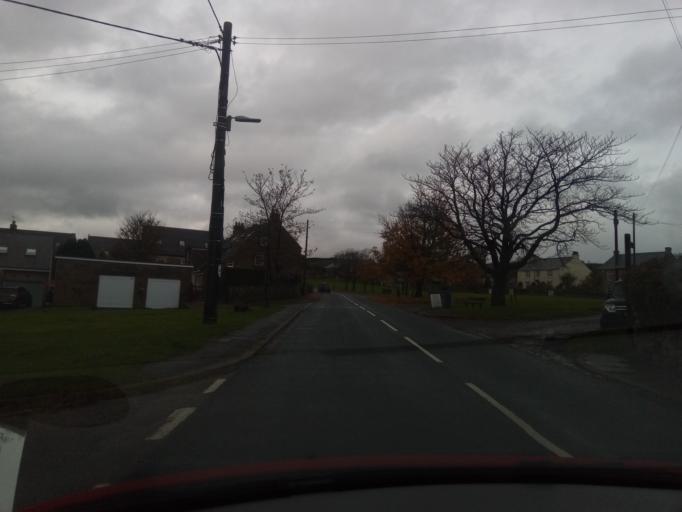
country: GB
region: England
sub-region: County Durham
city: Muggleswick
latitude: 54.8456
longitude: -1.9750
